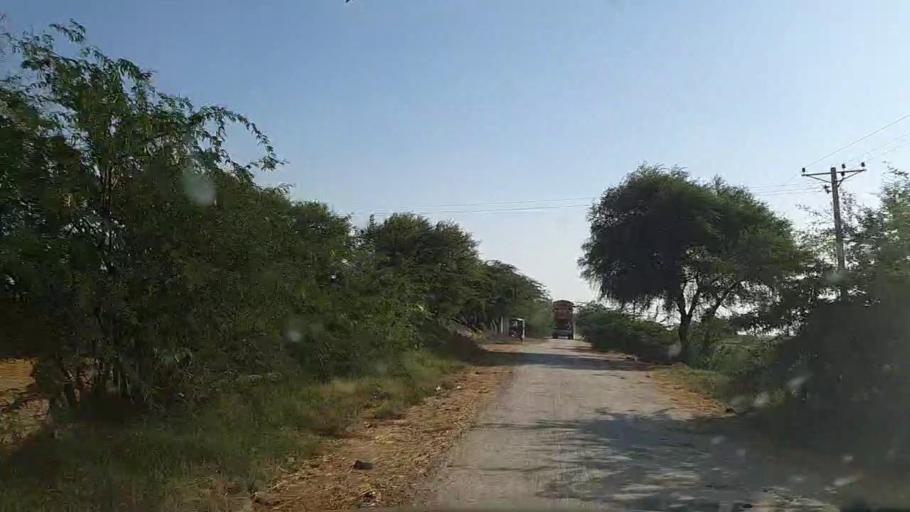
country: PK
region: Sindh
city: Daro Mehar
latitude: 24.6475
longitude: 68.0751
